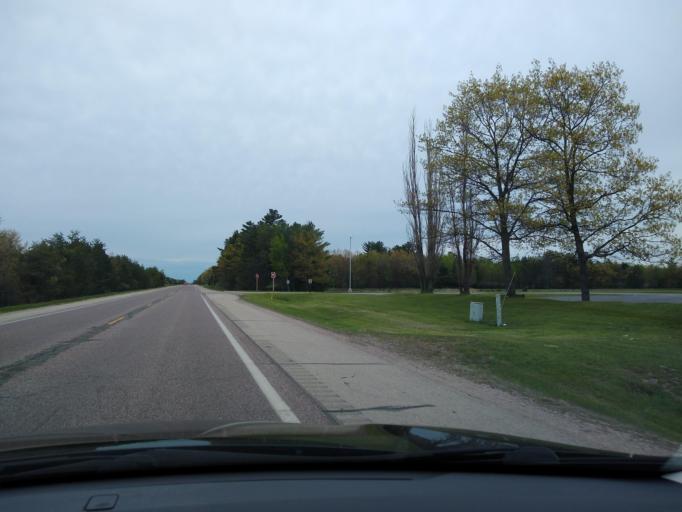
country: US
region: Michigan
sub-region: Delta County
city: Gladstone
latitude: 45.8670
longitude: -87.0631
